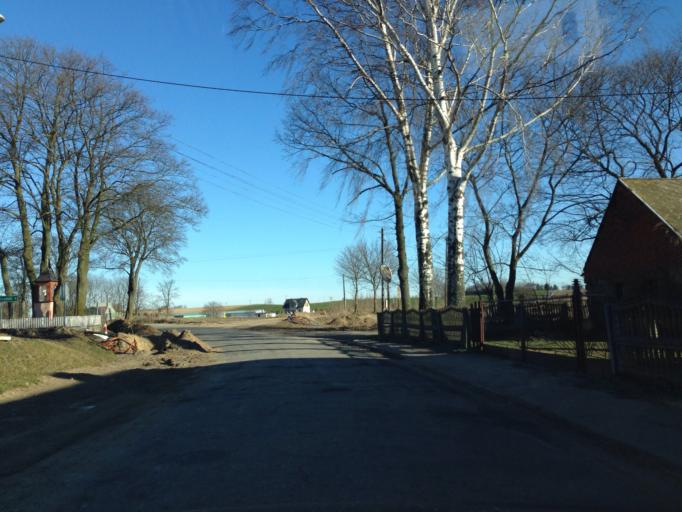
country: PL
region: Warmian-Masurian Voivodeship
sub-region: Powiat nowomiejski
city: Kurzetnik
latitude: 53.3764
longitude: 19.6277
